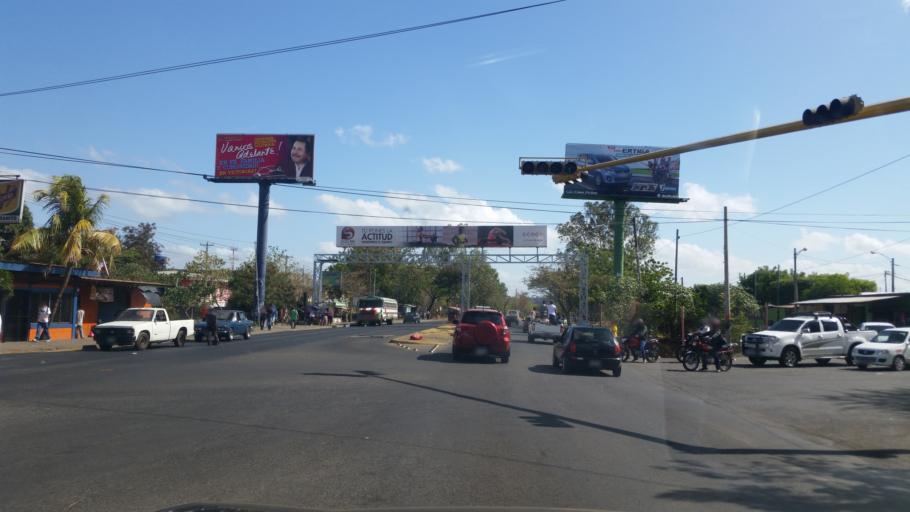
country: NI
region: Managua
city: Managua
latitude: 12.1383
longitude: -86.2277
